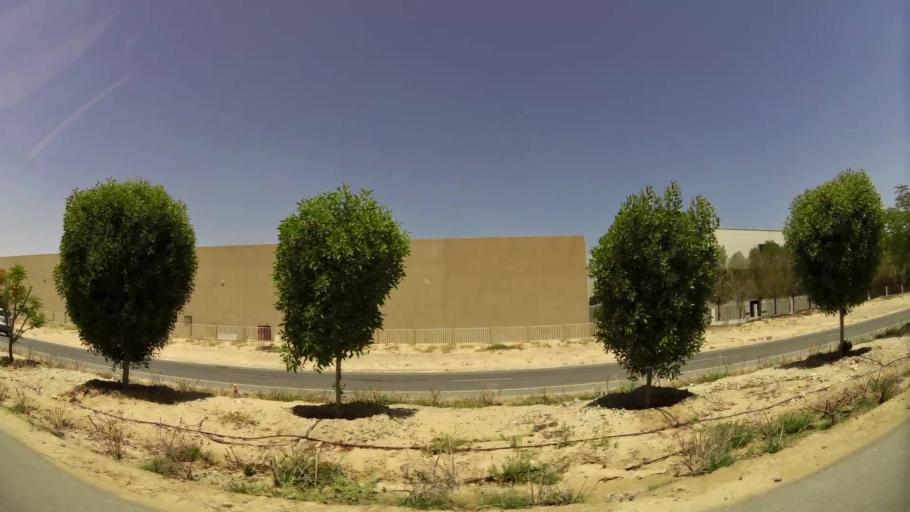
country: AE
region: Dubai
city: Dubai
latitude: 24.9687
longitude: 55.1978
